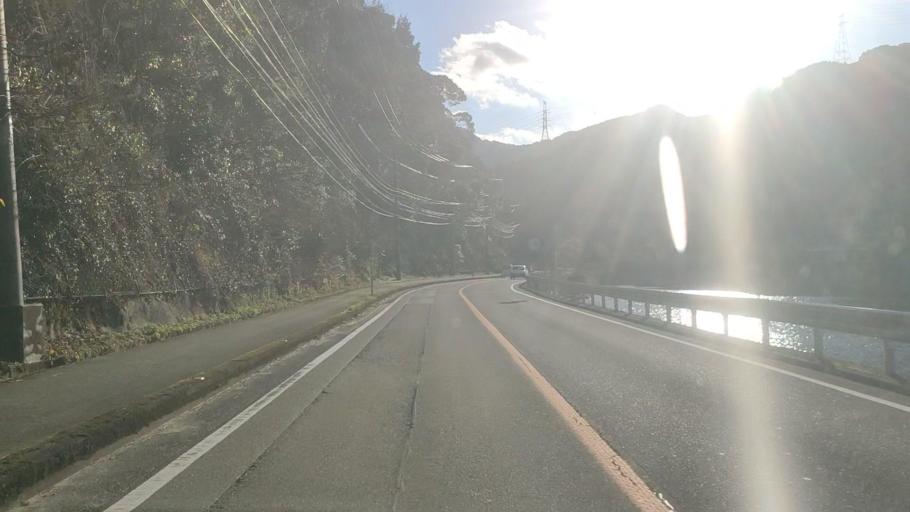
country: JP
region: Saga Prefecture
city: Saga-shi
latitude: 33.3479
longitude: 130.2494
